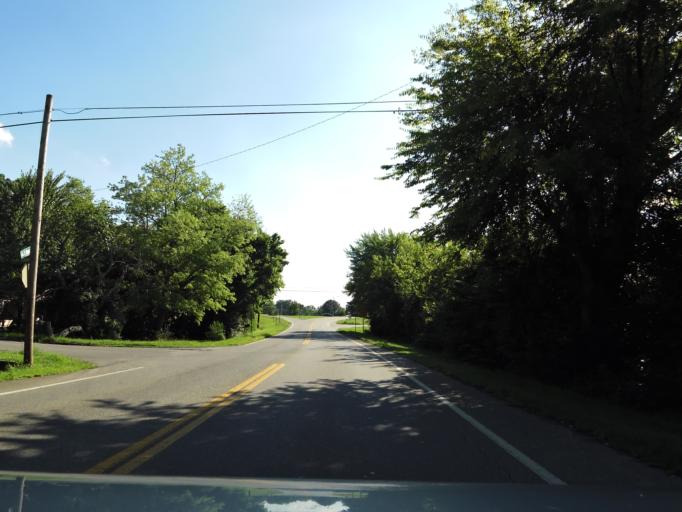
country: US
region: Tennessee
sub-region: Blount County
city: Alcoa
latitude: 35.8016
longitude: -83.9864
